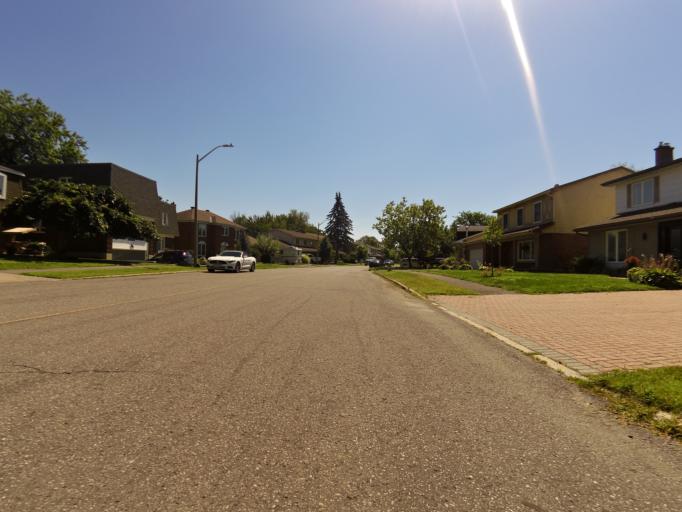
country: CA
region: Ontario
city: Ottawa
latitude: 45.3564
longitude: -75.6624
